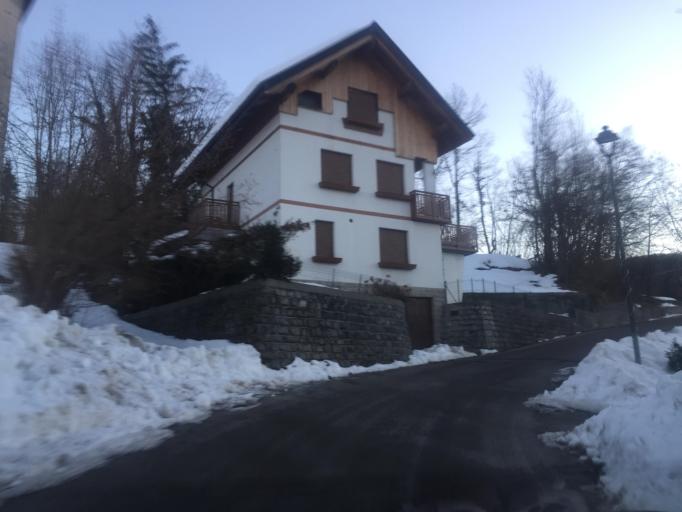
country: IT
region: Friuli Venezia Giulia
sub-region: Provincia di Udine
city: Lauco
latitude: 46.4264
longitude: 12.9333
